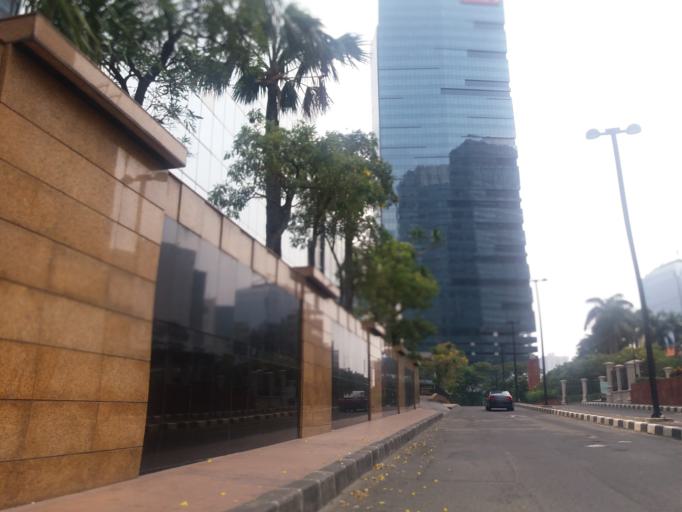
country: ID
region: Jakarta Raya
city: Jakarta
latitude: -6.2174
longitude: 106.8189
